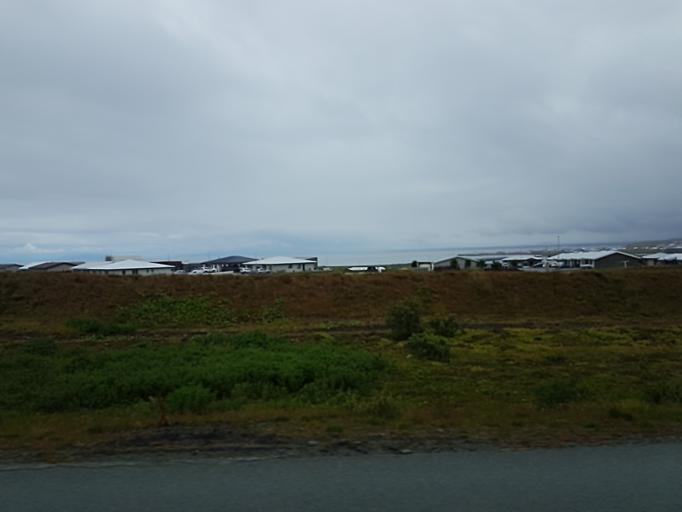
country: IS
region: Southern Peninsula
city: Reykjanesbaer
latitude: 63.9771
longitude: -22.5569
